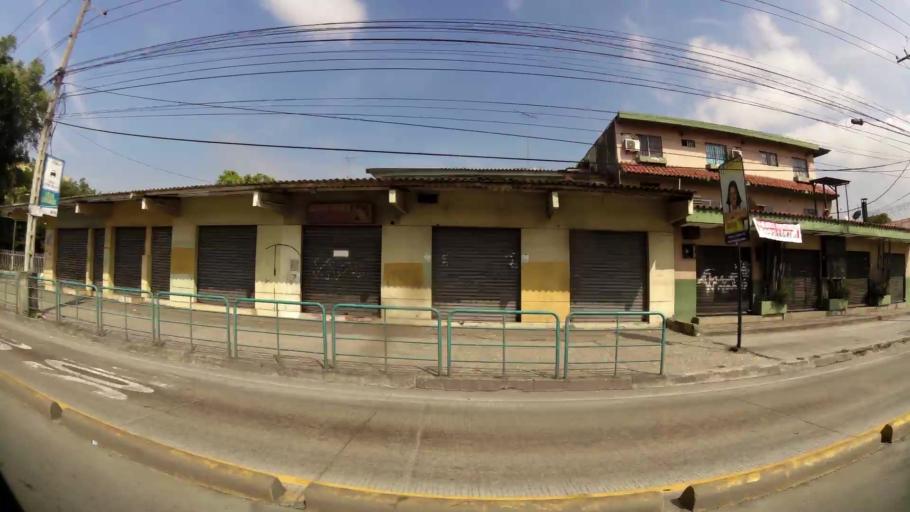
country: EC
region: Guayas
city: Guayaquil
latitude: -2.2412
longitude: -79.8962
